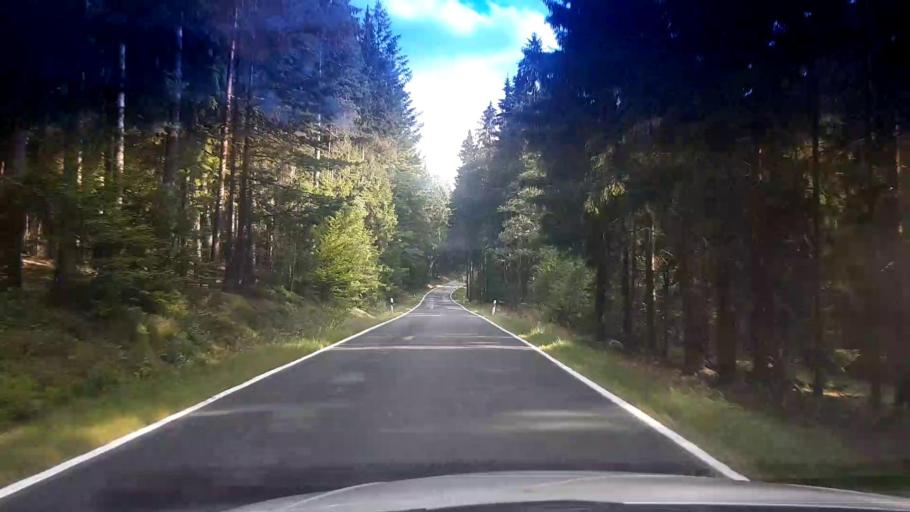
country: DE
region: Bavaria
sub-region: Upper Palatinate
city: Neualbenreuth
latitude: 49.9499
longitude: 12.4184
